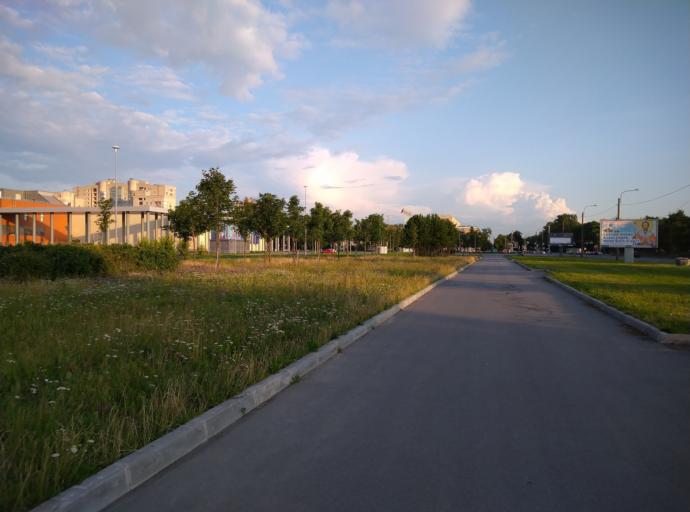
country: RU
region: St.-Petersburg
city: Kupchino
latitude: 59.8671
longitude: 30.3374
